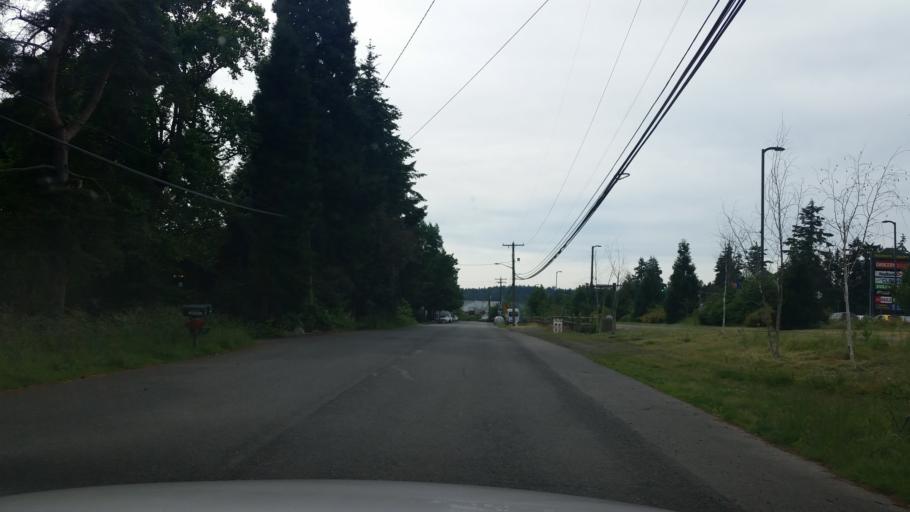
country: US
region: Washington
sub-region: King County
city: Kenmore
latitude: 47.7558
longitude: -122.2355
